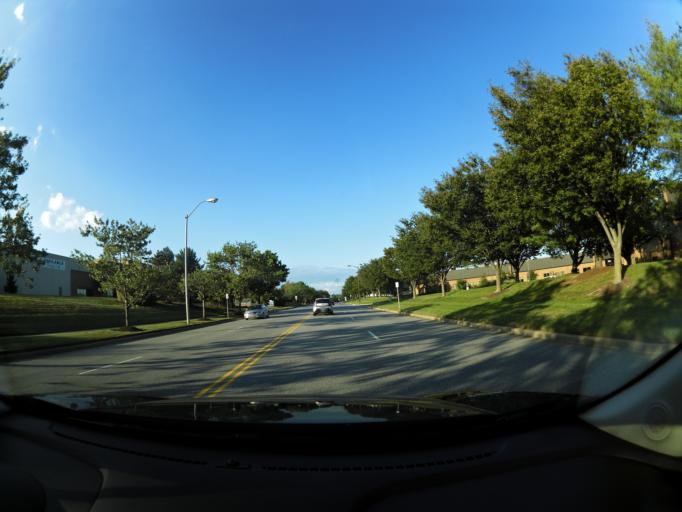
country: US
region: Maryland
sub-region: Howard County
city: Hanover
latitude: 39.1698
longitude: -76.7056
